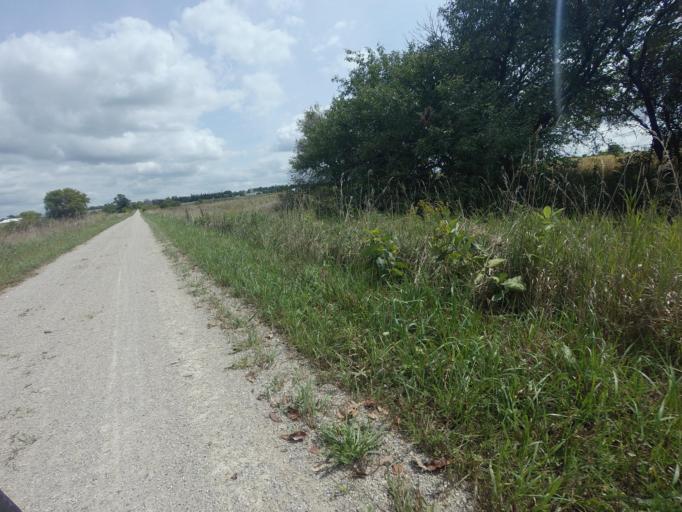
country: CA
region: Ontario
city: North Perth
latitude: 43.5672
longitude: -80.9372
